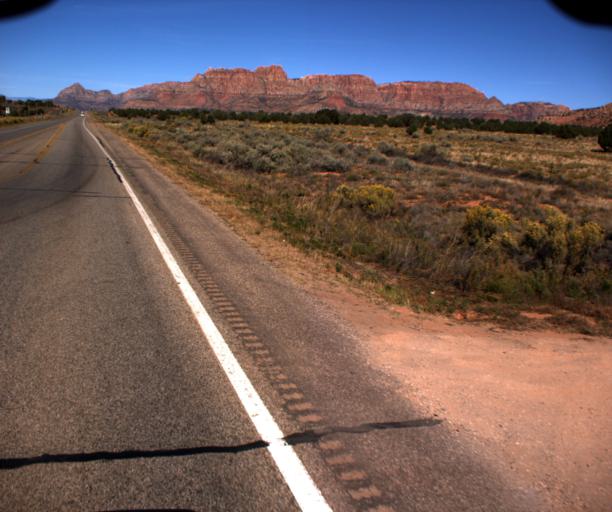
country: US
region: Arizona
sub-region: Mohave County
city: Colorado City
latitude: 36.9620
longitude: -112.9681
